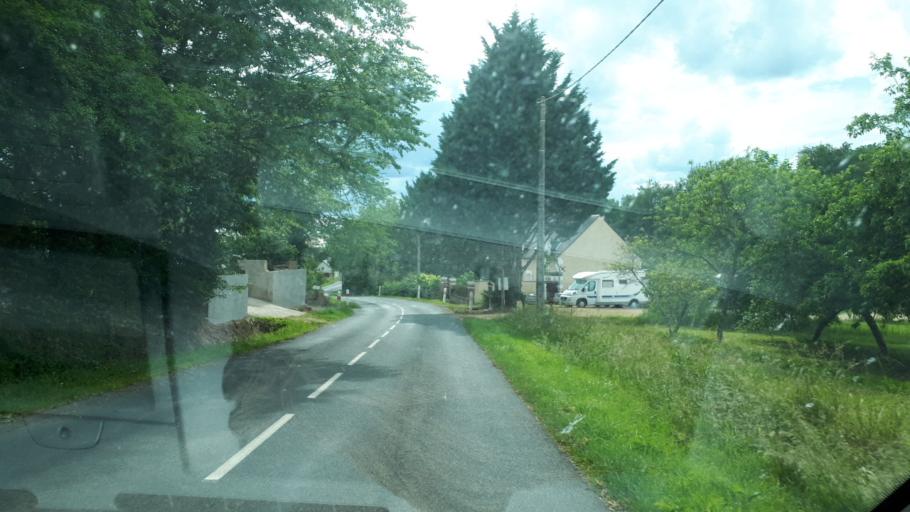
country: FR
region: Centre
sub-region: Departement du Cher
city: Gracay
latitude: 47.1371
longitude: 1.8759
